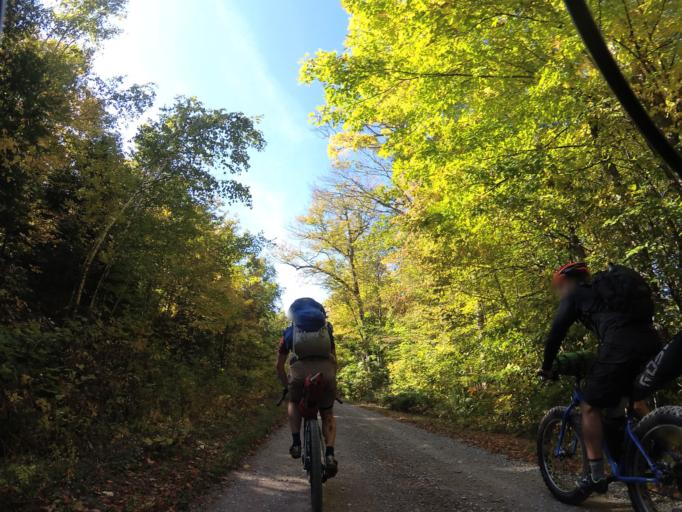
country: CA
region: Ontario
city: Renfrew
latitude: 45.3440
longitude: -77.0793
